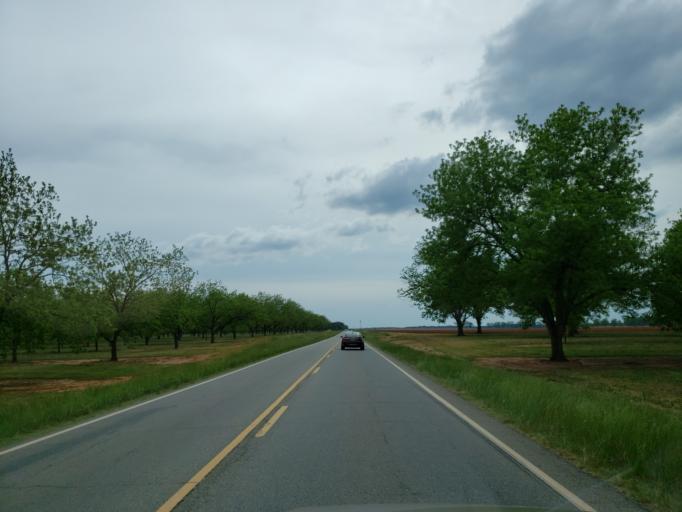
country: US
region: Georgia
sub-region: Houston County
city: Perry
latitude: 32.4354
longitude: -83.8017
